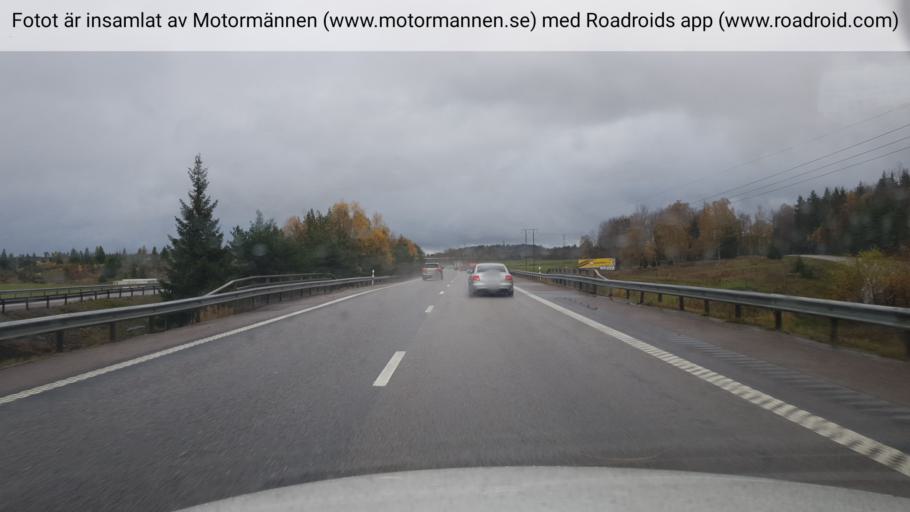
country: SE
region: Stockholm
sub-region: Sigtuna Kommun
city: Marsta
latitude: 59.6852
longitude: 17.8690
